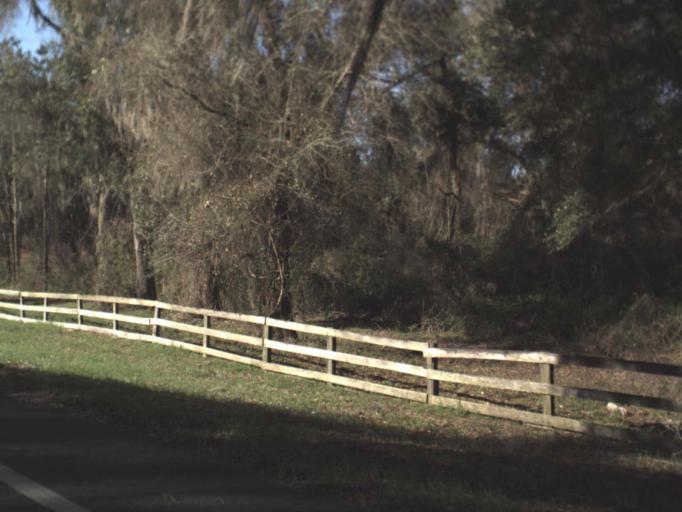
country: US
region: Georgia
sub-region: Brooks County
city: Quitman
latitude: 30.6406
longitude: -83.6442
